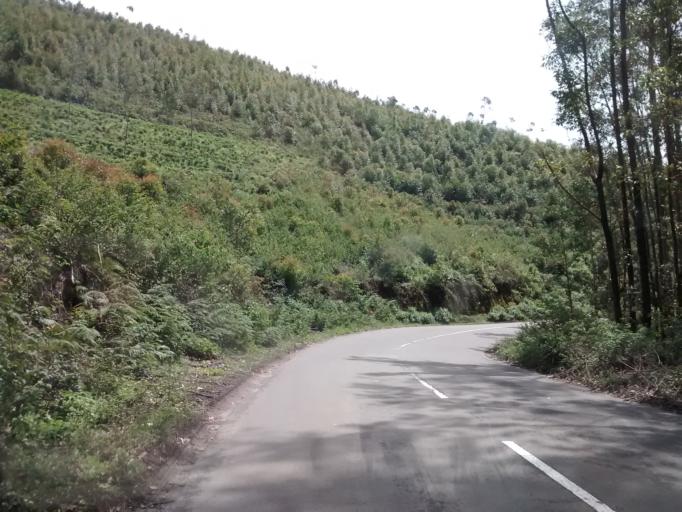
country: IN
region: Kerala
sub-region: Idukki
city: Munnar
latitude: 10.0996
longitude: 77.1070
